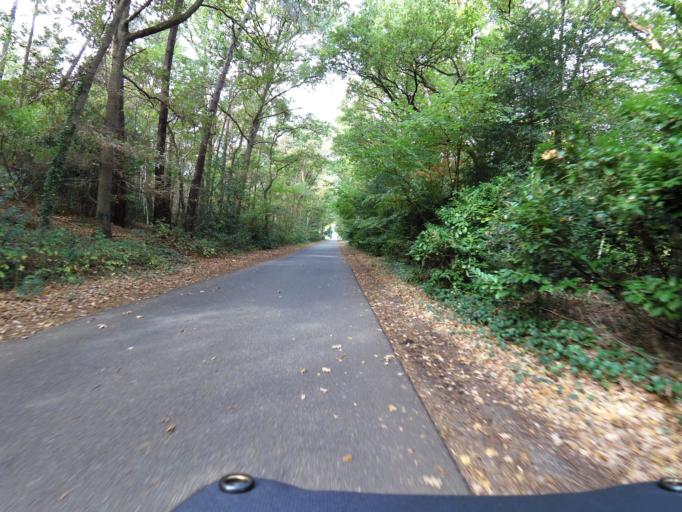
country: NL
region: North Brabant
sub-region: Gemeente Woensdrecht
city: Woensdrecht
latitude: 51.4291
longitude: 4.3863
